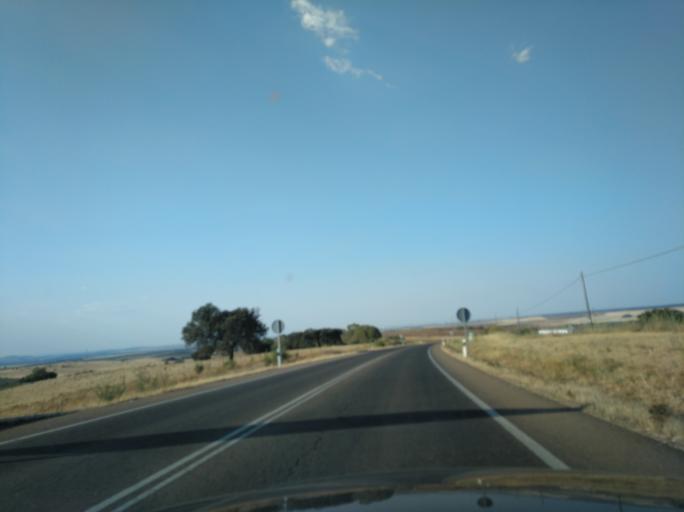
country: ES
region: Extremadura
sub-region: Provincia de Badajoz
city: Olivenza
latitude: 38.7184
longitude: -7.0838
